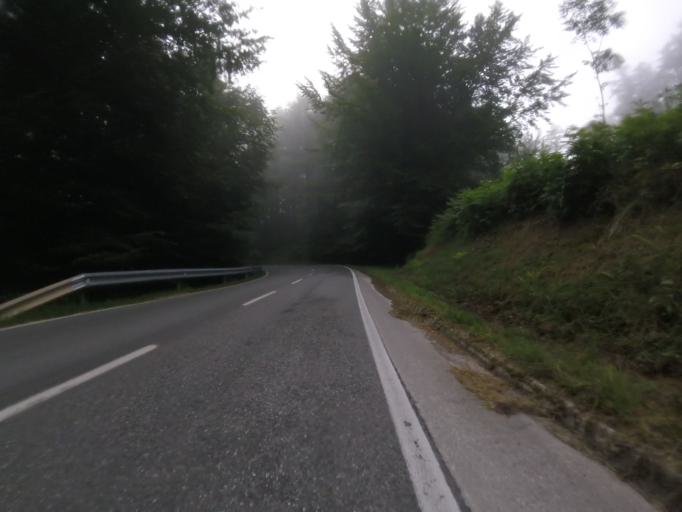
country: ES
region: Navarre
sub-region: Provincia de Navarra
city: Leitza
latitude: 43.0840
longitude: -1.8748
